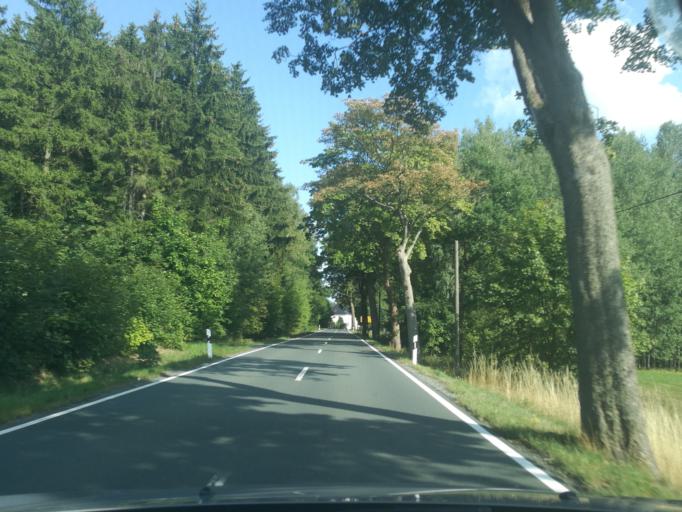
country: CZ
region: Karlovarsky
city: Hranice
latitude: 50.3230
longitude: 12.1622
